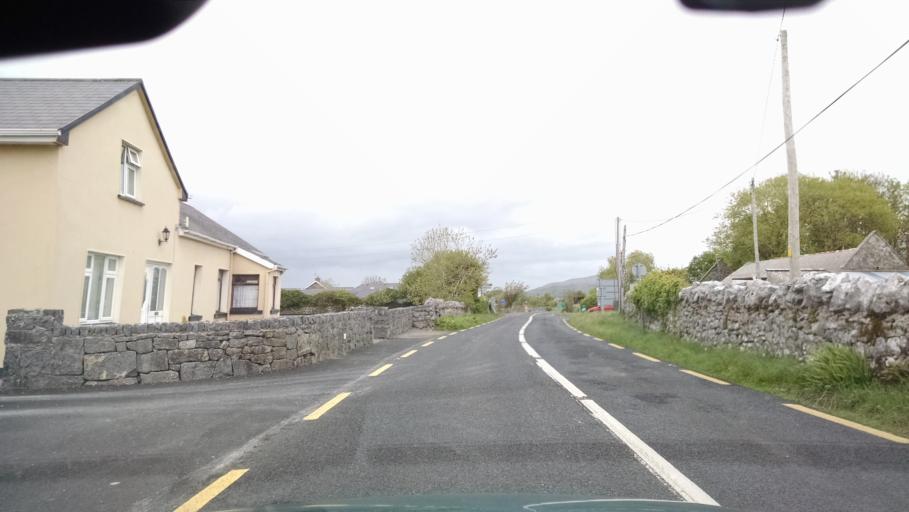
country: IE
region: Connaught
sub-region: County Galway
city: Bearna
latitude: 53.1031
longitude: -9.1611
